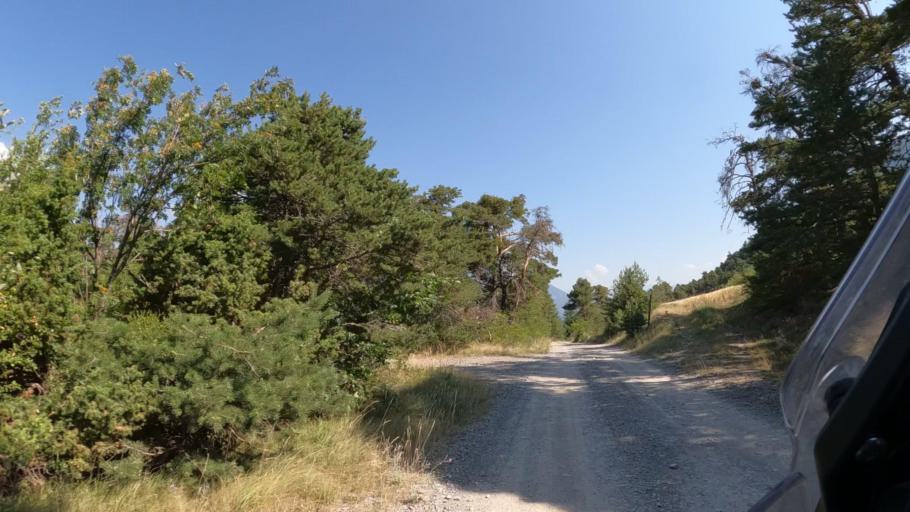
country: FR
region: Provence-Alpes-Cote d'Azur
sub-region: Departement des Hautes-Alpes
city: Embrun
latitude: 44.5874
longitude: 6.5496
